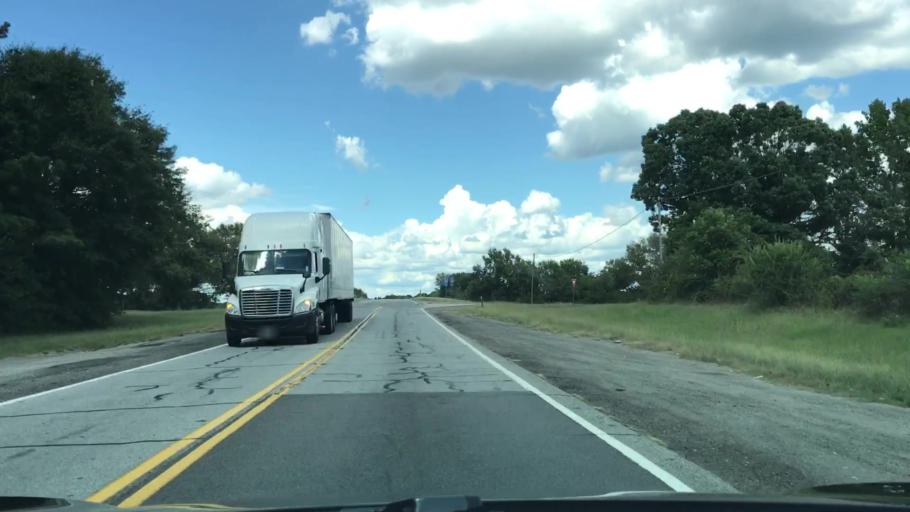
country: US
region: Georgia
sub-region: Greene County
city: Union Point
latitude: 33.5418
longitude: -83.0802
